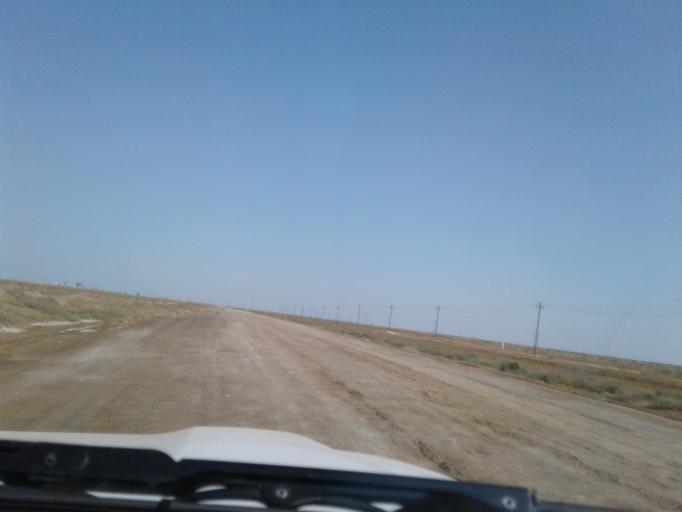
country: IR
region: Golestan
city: Gomishan
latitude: 37.7518
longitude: 53.9299
